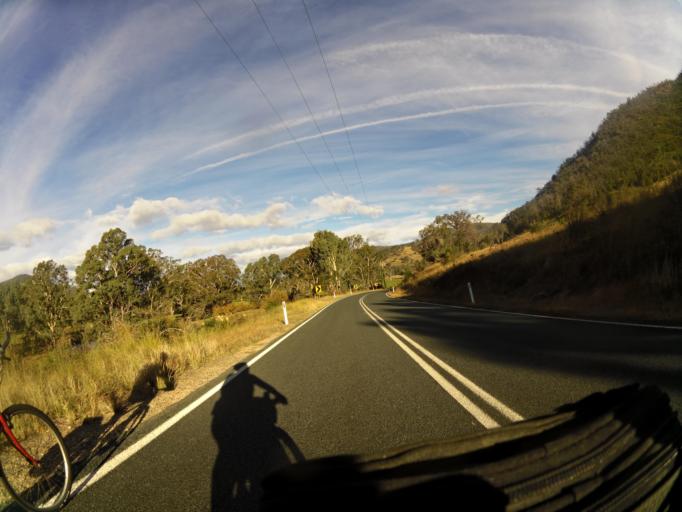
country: AU
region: New South Wales
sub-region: Greater Hume Shire
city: Holbrook
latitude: -35.9944
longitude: 147.8647
